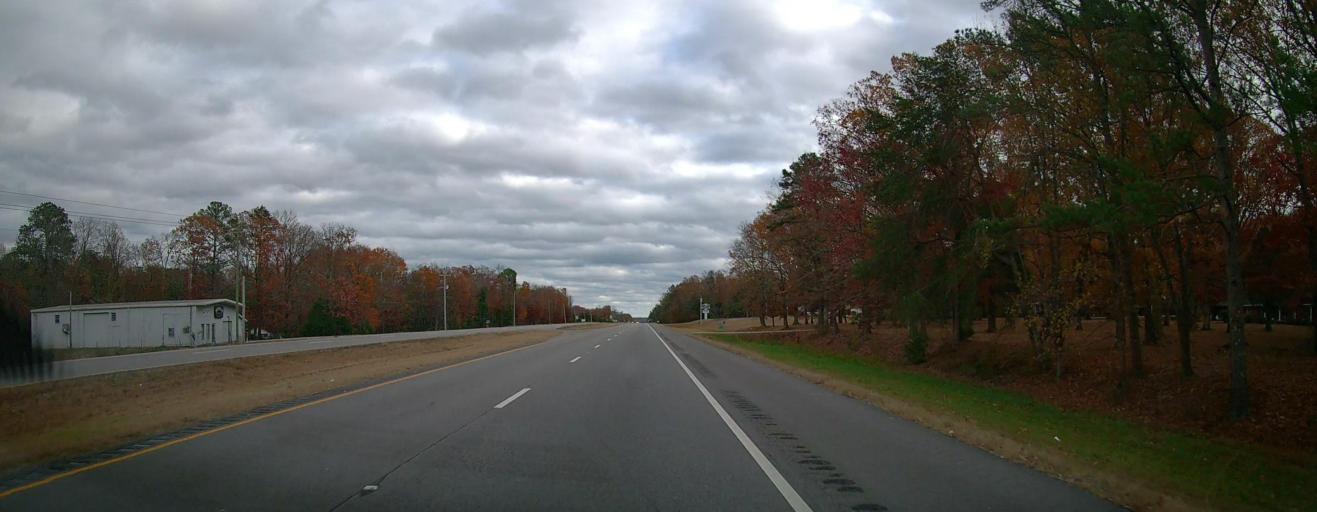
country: US
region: Alabama
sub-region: Colbert County
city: Muscle Shoals
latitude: 34.6677
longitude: -87.5567
